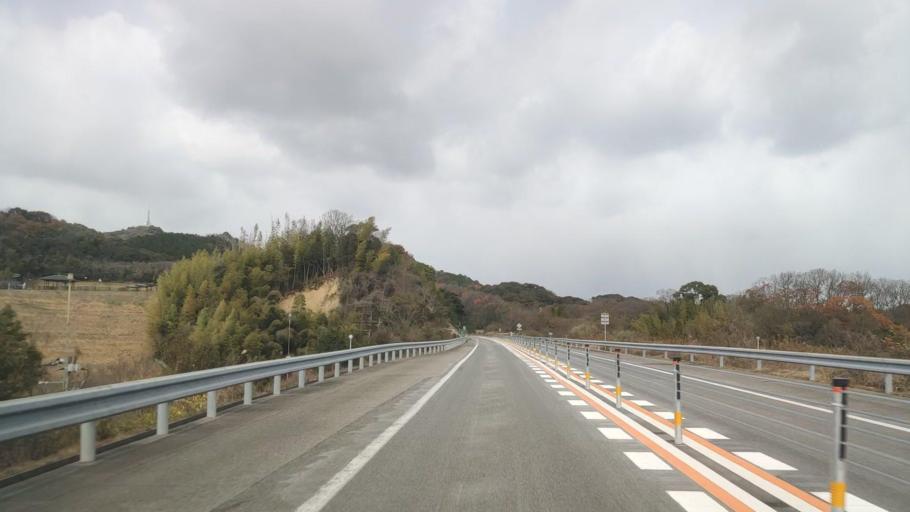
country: JP
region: Ehime
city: Hojo
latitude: 34.0722
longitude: 132.9750
